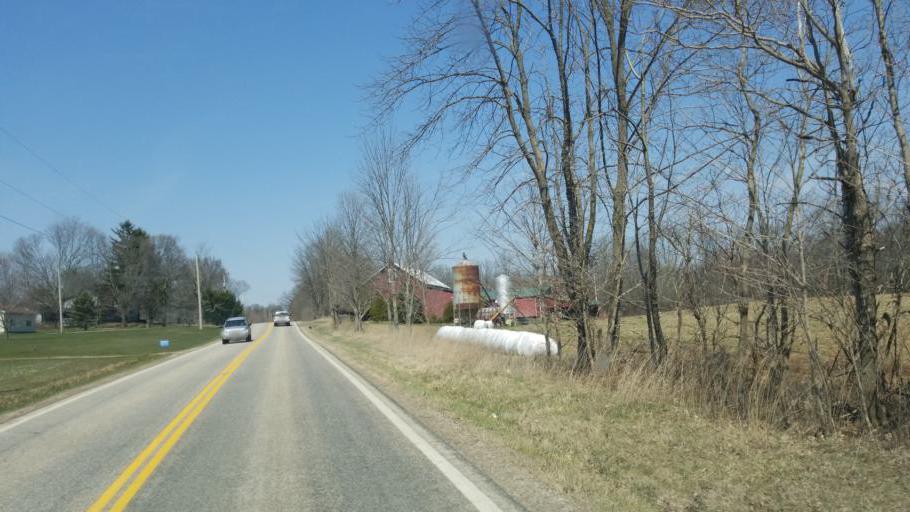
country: US
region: Ohio
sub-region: Ashland County
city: Loudonville
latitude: 40.7417
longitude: -82.2047
